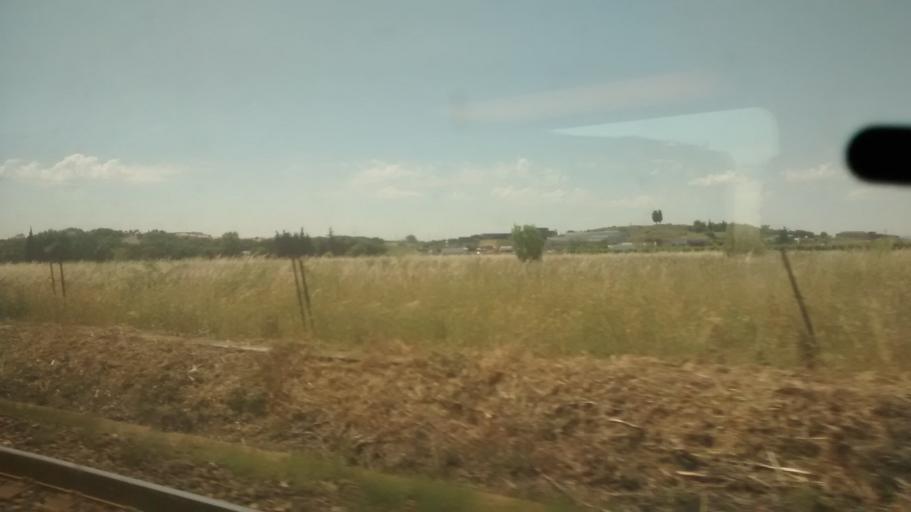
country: FR
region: Languedoc-Roussillon
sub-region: Departement de l'Herault
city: Saint-Aunes
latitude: 43.6446
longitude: 3.9843
